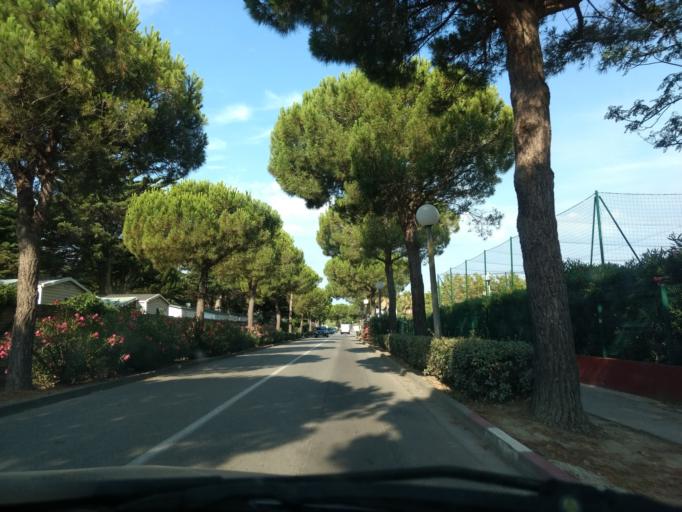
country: FR
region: Languedoc-Roussillon
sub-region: Departement des Pyrenees-Orientales
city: Le Barcares
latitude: 42.7764
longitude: 3.0262
